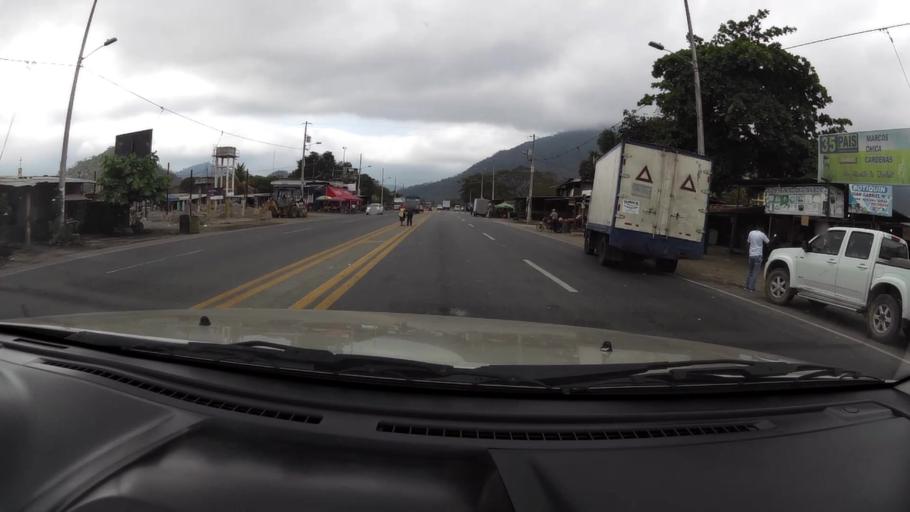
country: EC
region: Guayas
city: Coronel Marcelino Mariduena
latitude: -2.3835
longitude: -79.6312
